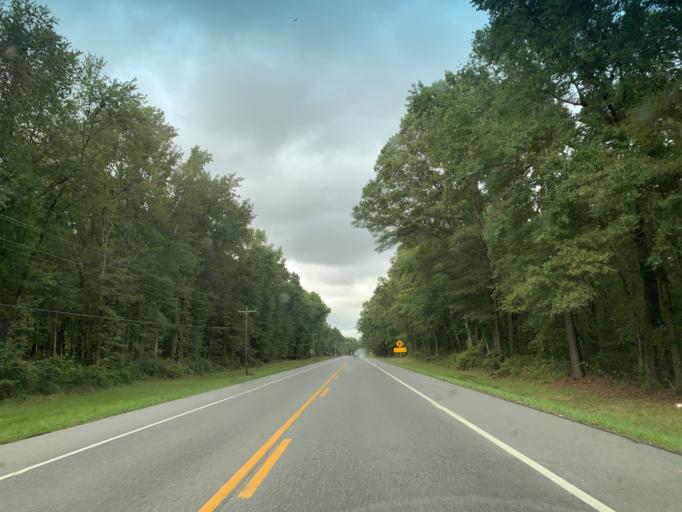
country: US
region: Maryland
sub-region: Caroline County
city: Ridgely
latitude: 39.0169
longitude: -75.8746
